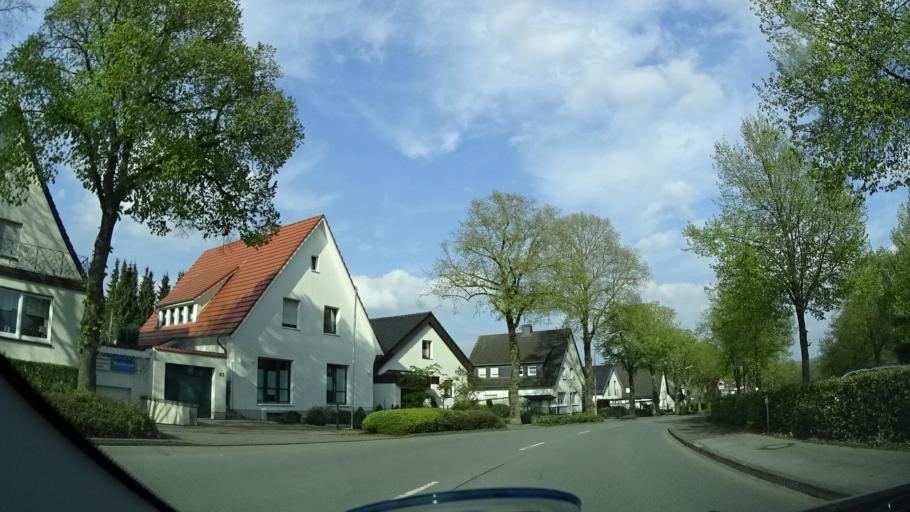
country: DE
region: North Rhine-Westphalia
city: Warstein
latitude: 51.4430
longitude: 8.3419
